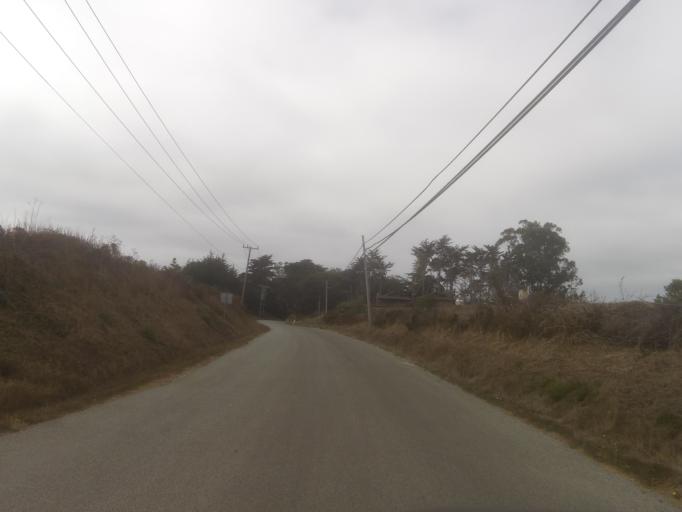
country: US
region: California
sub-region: San Mateo County
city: Half Moon Bay
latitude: 37.4042
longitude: -122.4140
